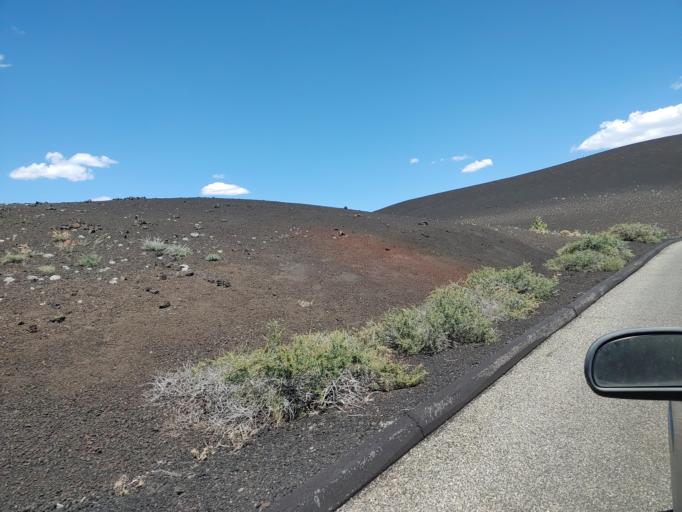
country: US
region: Idaho
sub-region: Butte County
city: Arco
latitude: 43.4433
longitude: -113.5560
